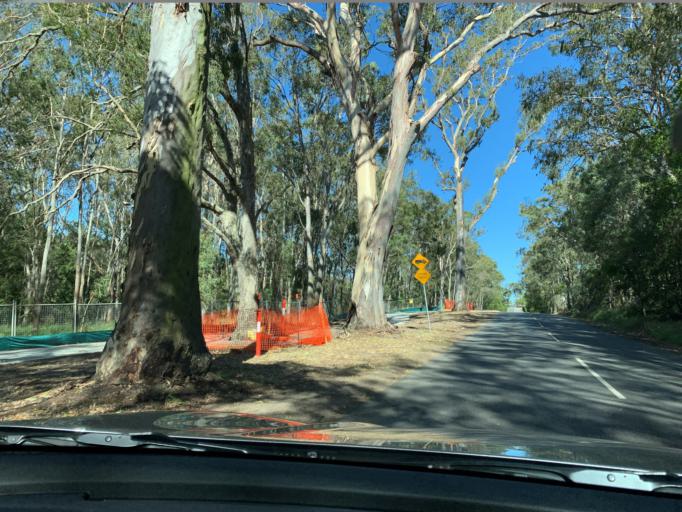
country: AU
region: Queensland
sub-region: Brisbane
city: Wynnum
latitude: -27.4263
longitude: 153.1592
